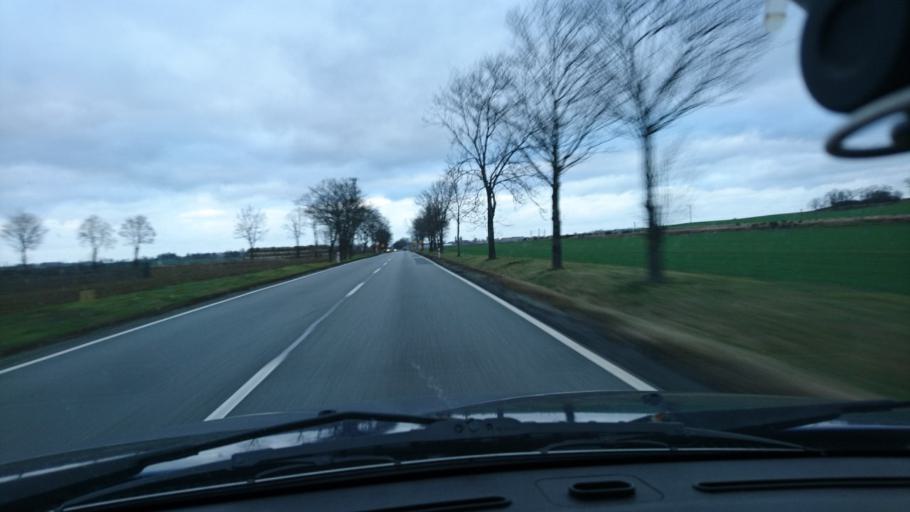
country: PL
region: Opole Voivodeship
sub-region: Powiat kluczborski
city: Byczyna
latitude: 51.0945
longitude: 18.2025
